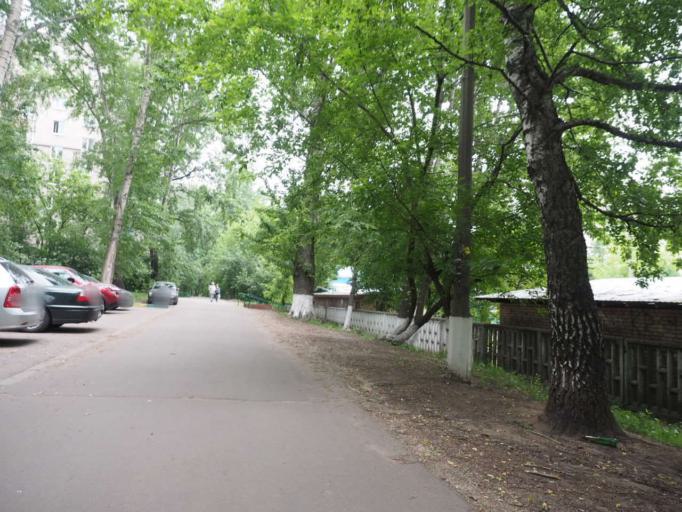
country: RU
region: Moskovskaya
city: Lyubertsy
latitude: 55.6614
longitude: 37.9004
